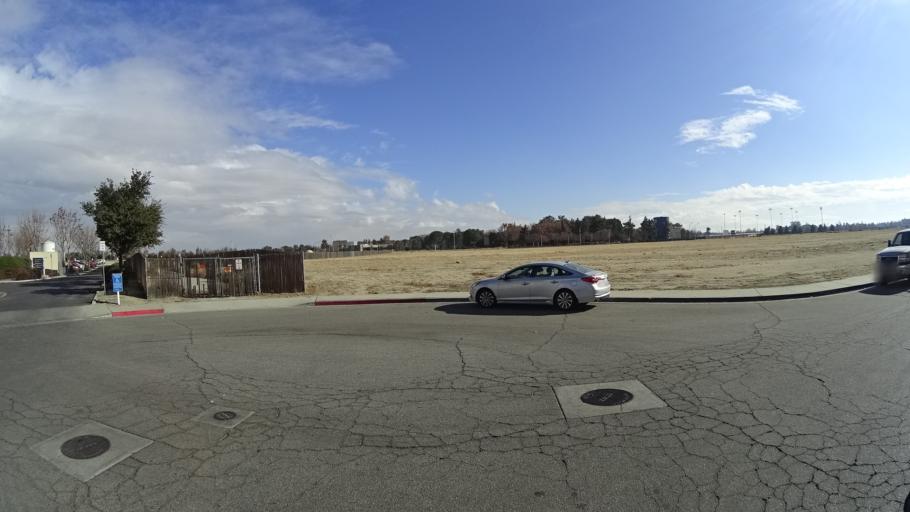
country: US
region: California
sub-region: Kern County
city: Greenacres
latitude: 35.3505
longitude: -119.1121
